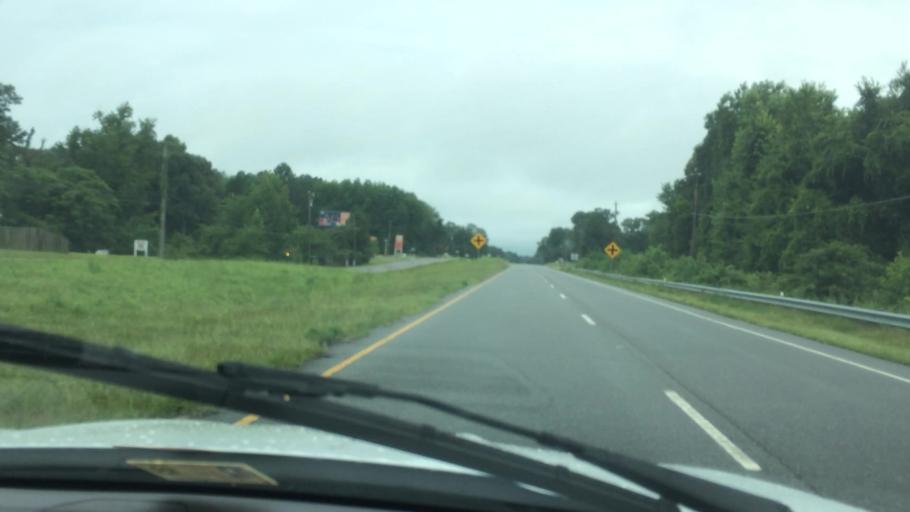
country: US
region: Virginia
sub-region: King William County
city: West Point
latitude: 37.5430
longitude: -76.7498
